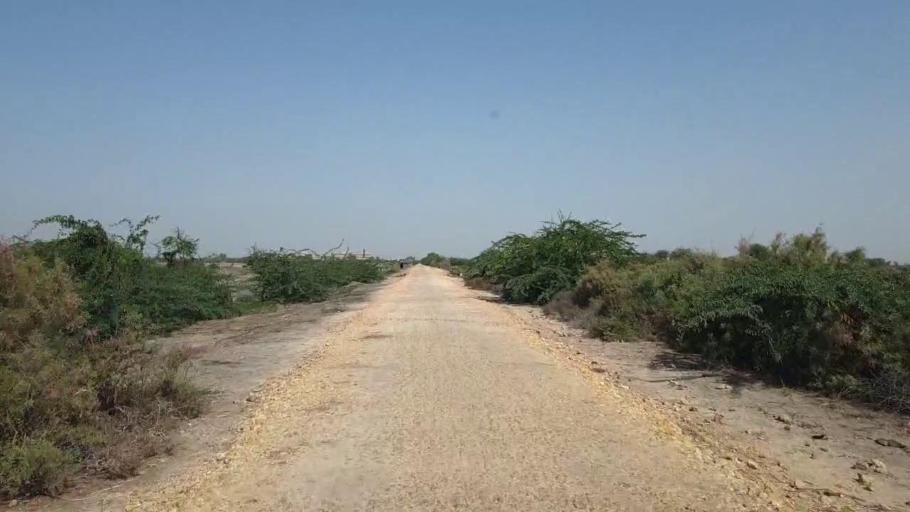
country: PK
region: Sindh
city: Tando Bago
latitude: 24.7314
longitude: 69.0741
